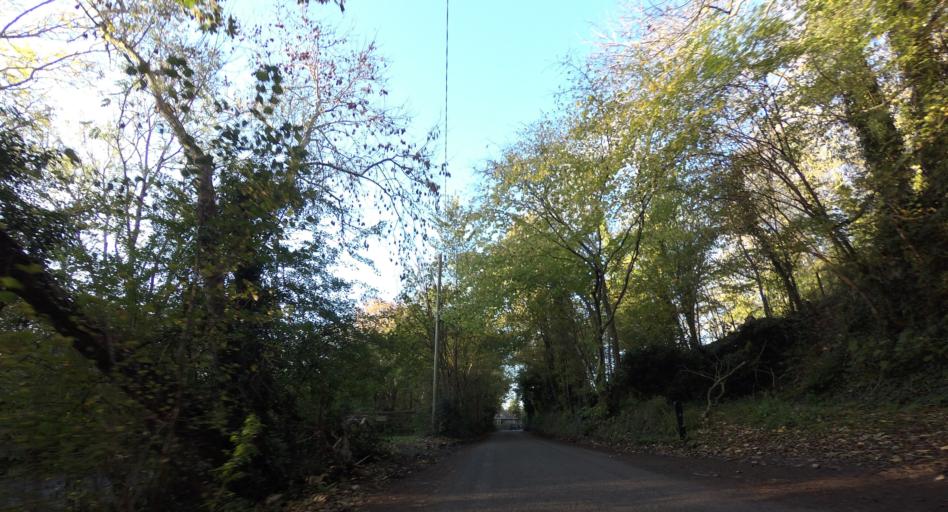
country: GB
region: England
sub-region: West Sussex
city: Steyning
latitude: 50.8832
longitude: -0.3177
